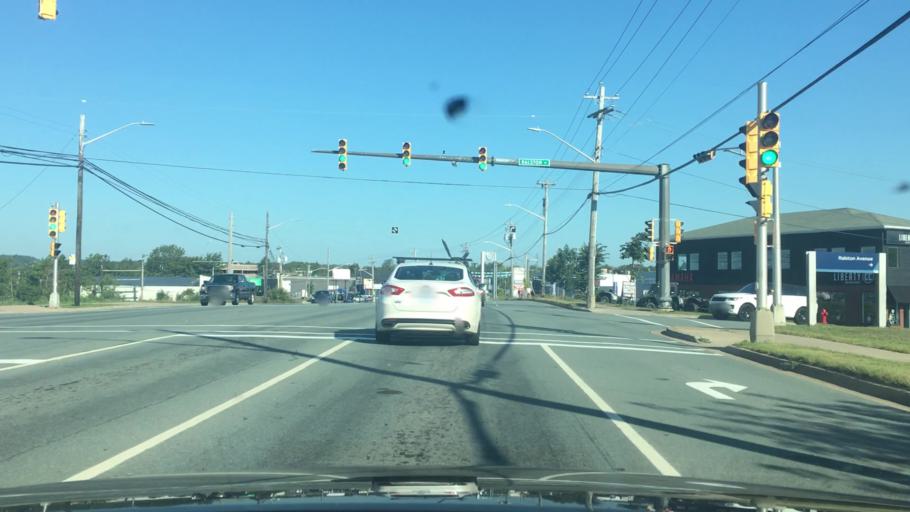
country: CA
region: Nova Scotia
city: Dartmouth
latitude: 44.7006
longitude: -63.6068
